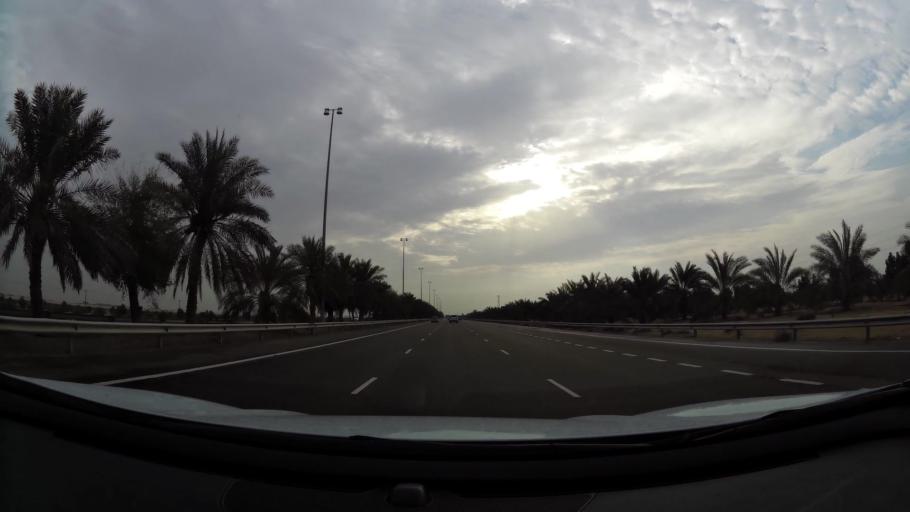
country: AE
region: Abu Dhabi
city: Abu Dhabi
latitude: 24.2247
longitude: 54.8043
